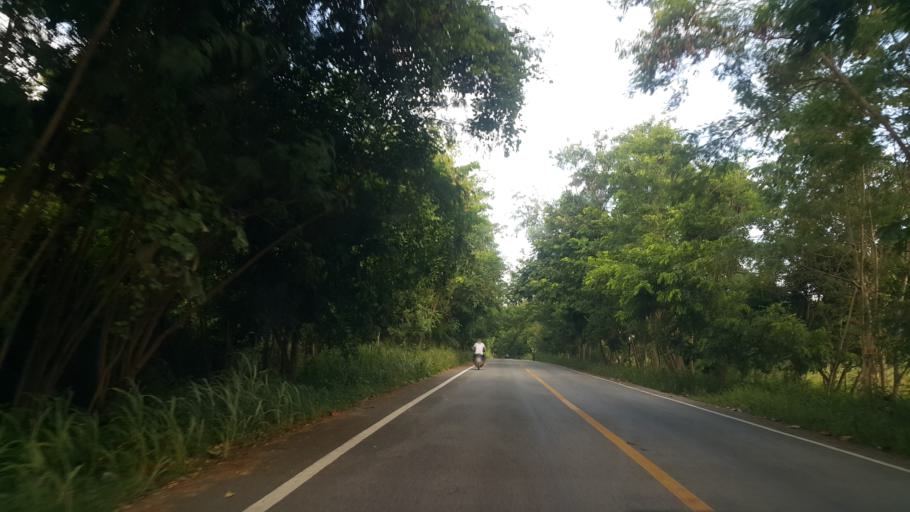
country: TH
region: Rayong
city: Ban Chang
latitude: 12.7838
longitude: 100.9611
